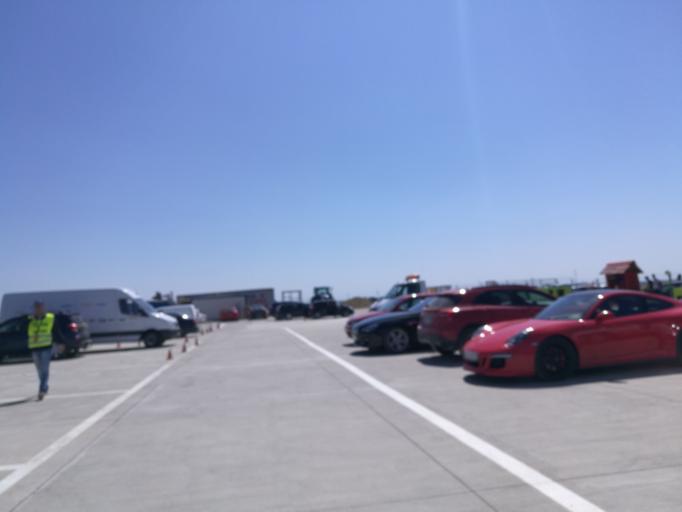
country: RO
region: Prahova
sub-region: Comuna Salciile
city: Salciile
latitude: 44.7789
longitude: 26.4723
